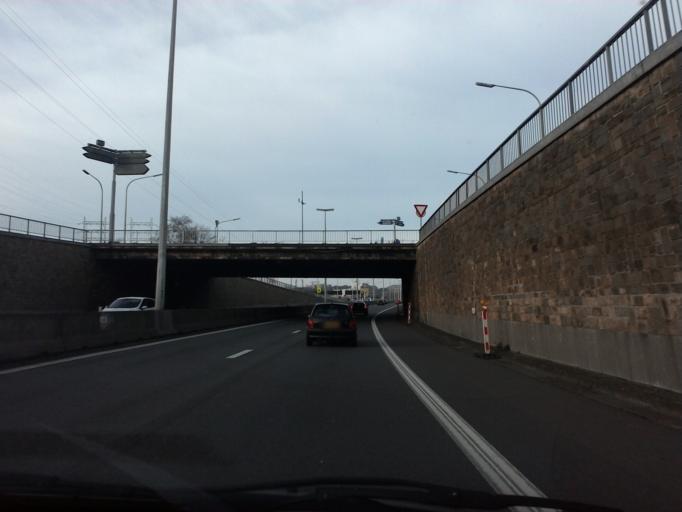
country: BE
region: Wallonia
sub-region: Province de Liege
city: Herstal
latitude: 50.6504
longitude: 5.6313
